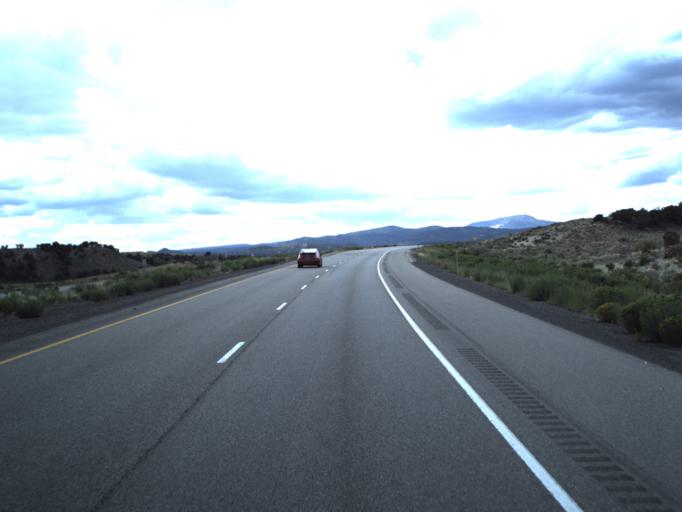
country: US
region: Utah
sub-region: Emery County
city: Ferron
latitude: 38.7832
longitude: -111.3056
